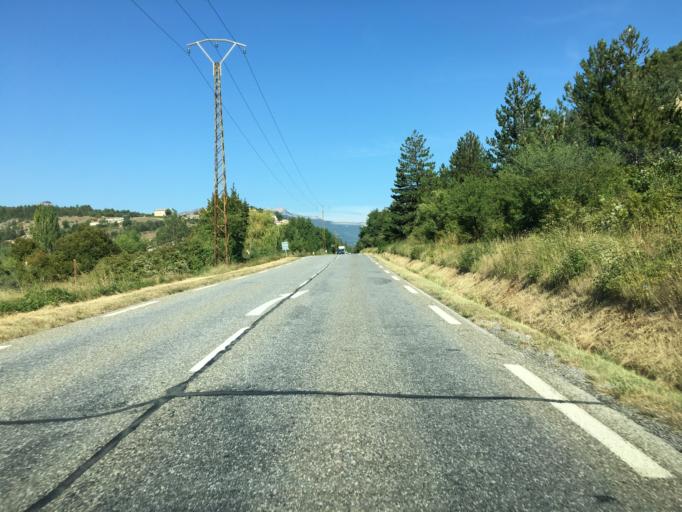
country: FR
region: Provence-Alpes-Cote d'Azur
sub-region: Departement des Hautes-Alpes
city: Laragne-Monteglin
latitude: 44.3353
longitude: 5.7837
